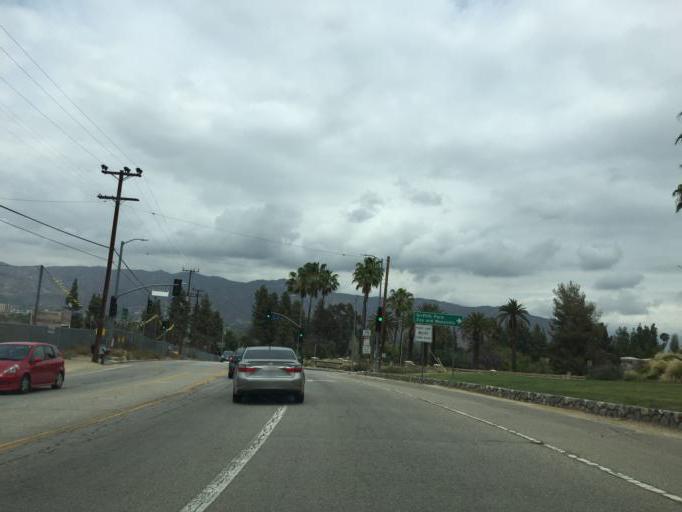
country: US
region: California
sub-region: Los Angeles County
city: Burbank
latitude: 34.1527
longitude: -118.3121
